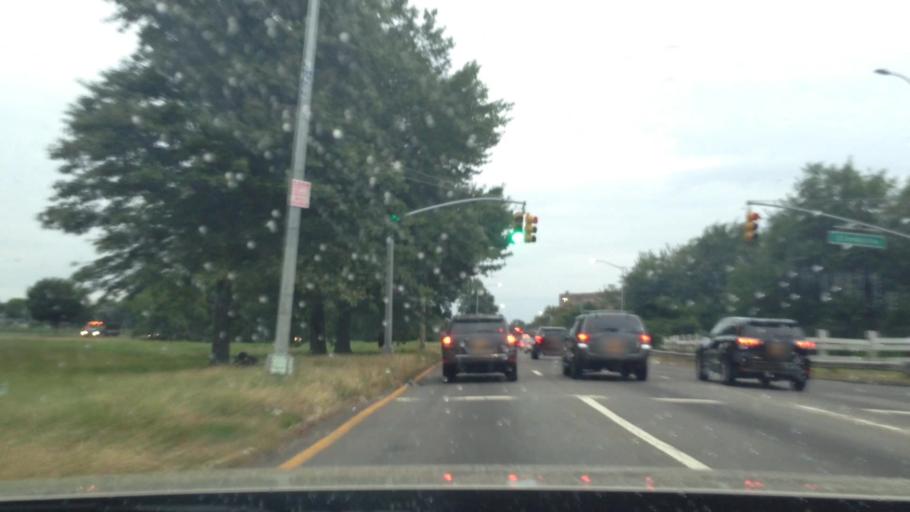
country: US
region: New York
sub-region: Queens County
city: Borough of Queens
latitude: 40.6713
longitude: -73.8516
